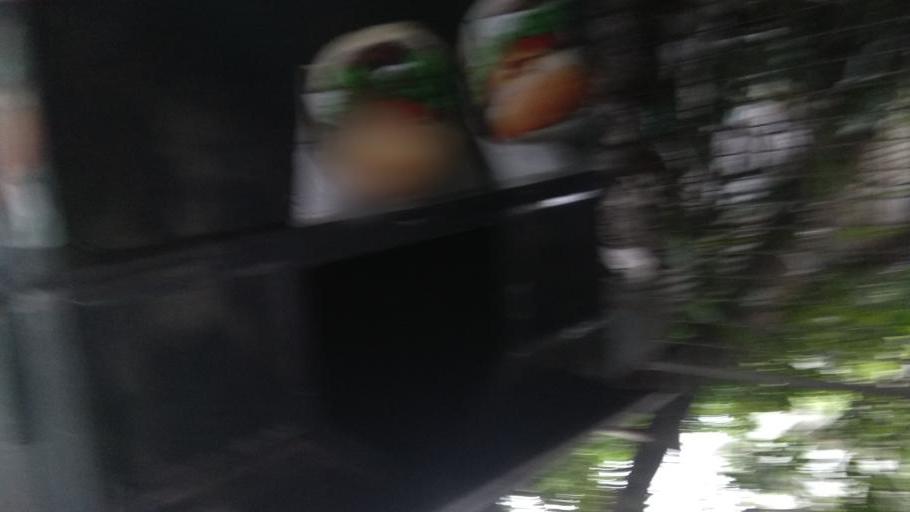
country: BD
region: Dhaka
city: Azimpur
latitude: 23.7984
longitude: 90.3844
